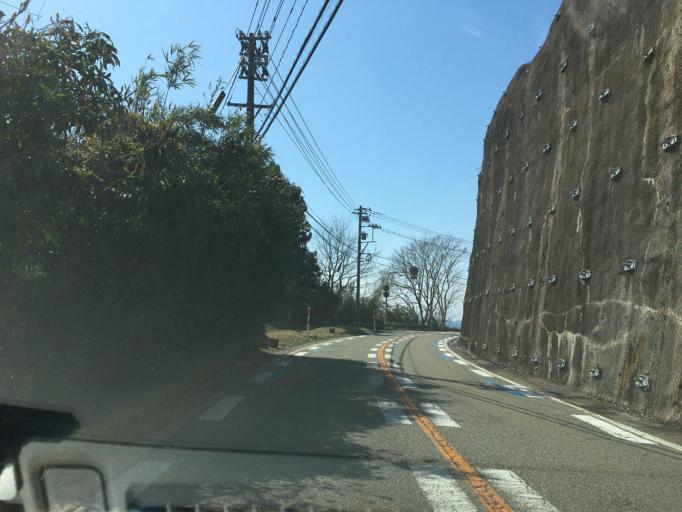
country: JP
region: Toyama
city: Himi
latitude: 36.9059
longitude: 137.0146
